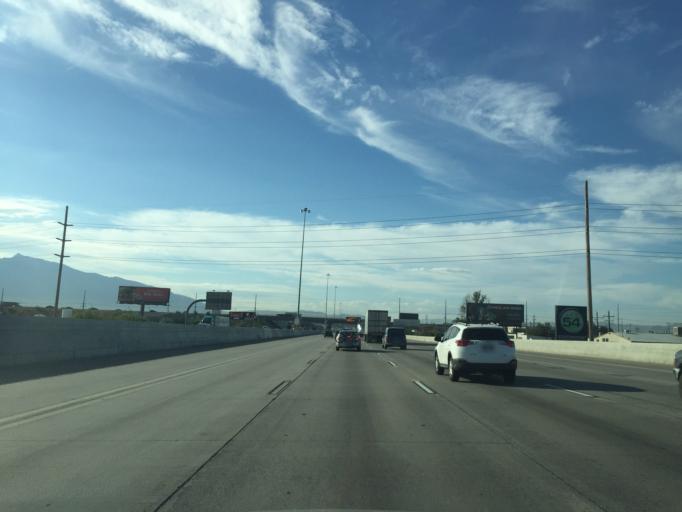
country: US
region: Utah
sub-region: Salt Lake County
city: Centerfield
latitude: 40.6900
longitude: -111.9033
